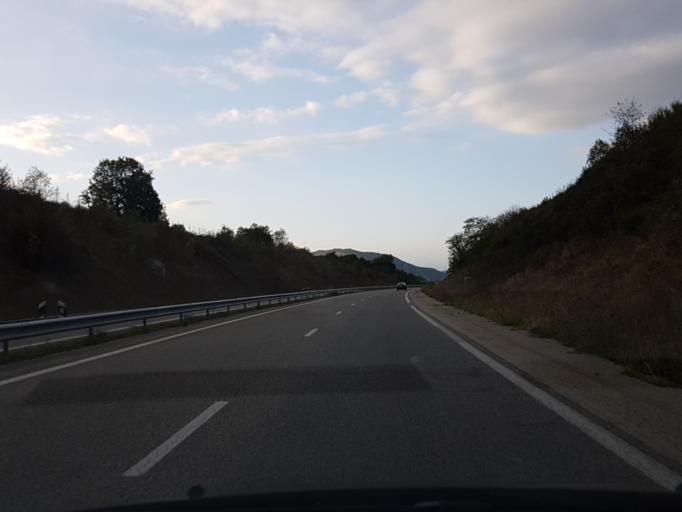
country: FR
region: Midi-Pyrenees
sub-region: Departement de l'Ariege
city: Montgaillard
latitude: 42.9337
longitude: 1.6273
